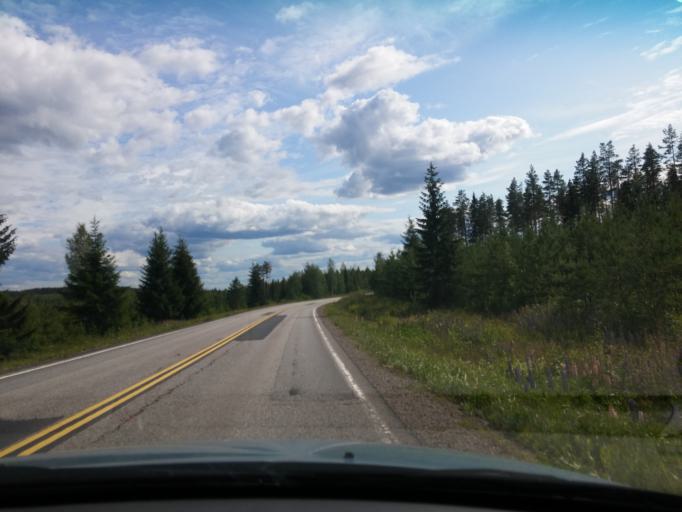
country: FI
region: Central Finland
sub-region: Keuruu
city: Keuruu
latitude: 62.3243
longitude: 24.7337
